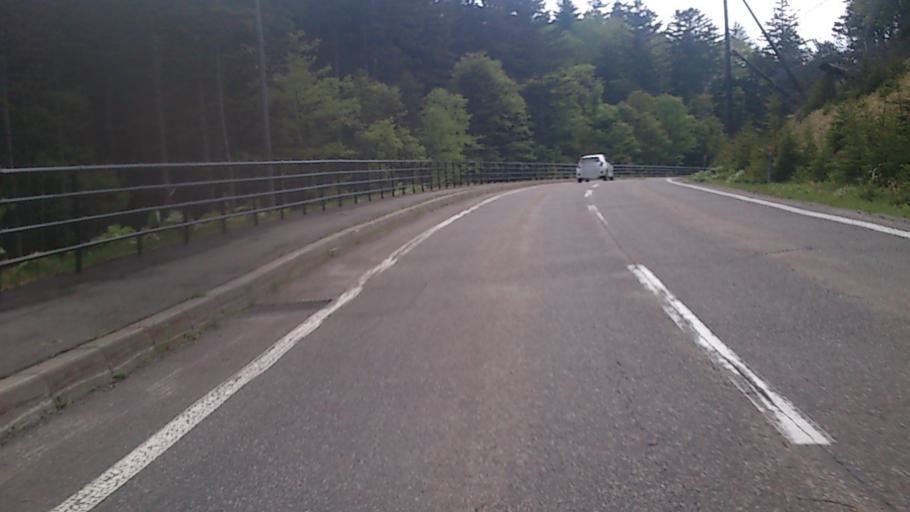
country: JP
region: Hokkaido
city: Kitami
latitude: 43.3951
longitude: 143.9823
